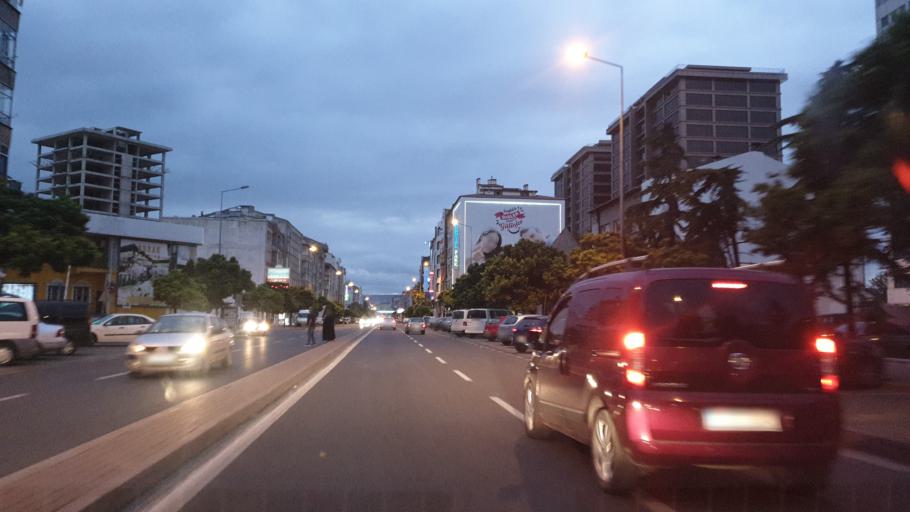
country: TR
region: Kayseri
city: Kayseri
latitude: 38.7220
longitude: 35.4821
